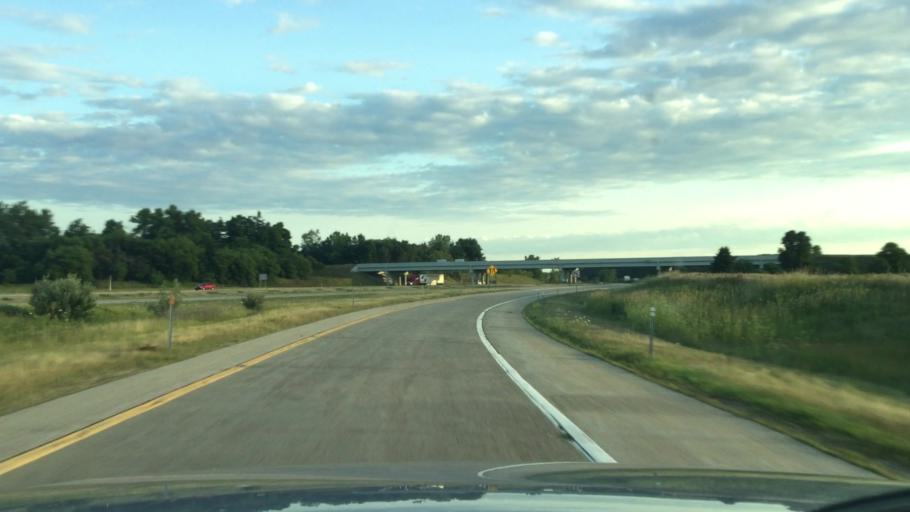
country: US
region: Michigan
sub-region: Clinton County
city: Bath
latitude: 42.8104
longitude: -84.5104
